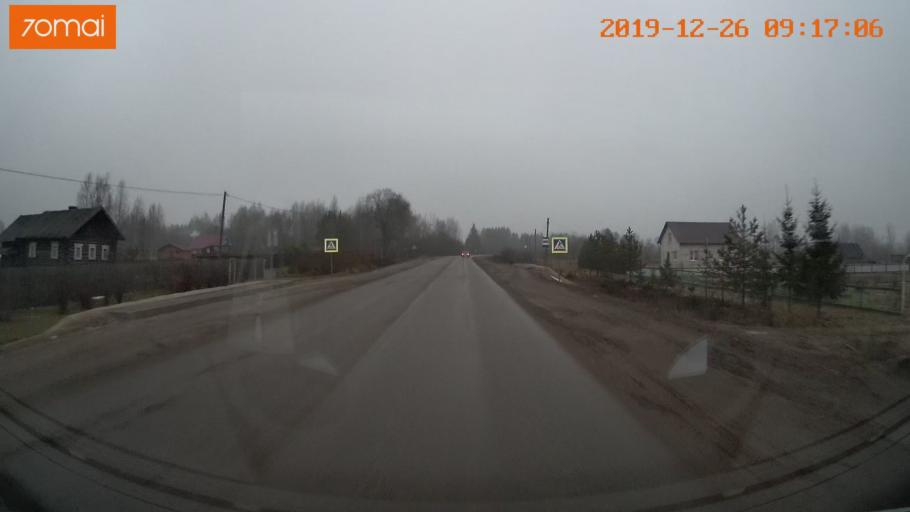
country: RU
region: Vologda
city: Gryazovets
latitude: 58.9259
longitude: 40.2389
